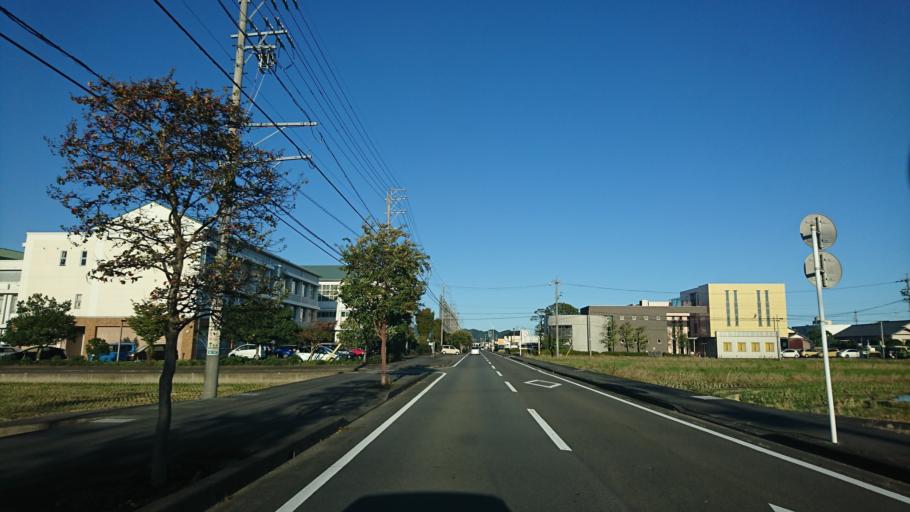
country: JP
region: Shizuoka
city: Fujieda
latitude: 34.8664
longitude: 138.2708
